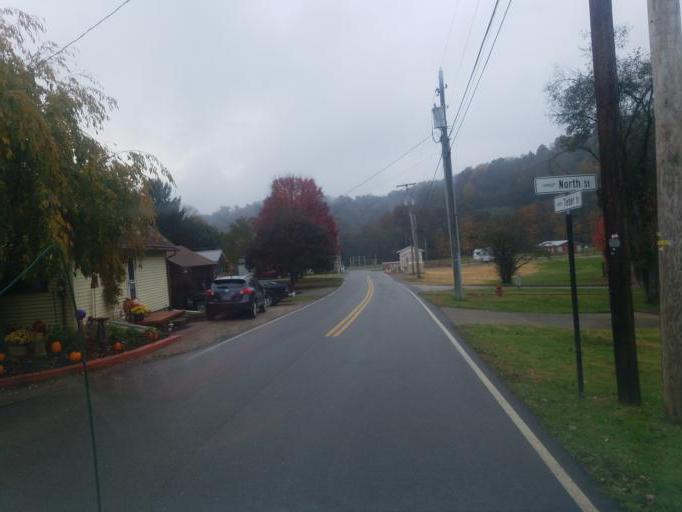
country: US
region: Ohio
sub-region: Morgan County
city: McConnelsville
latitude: 39.5499
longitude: -81.7986
